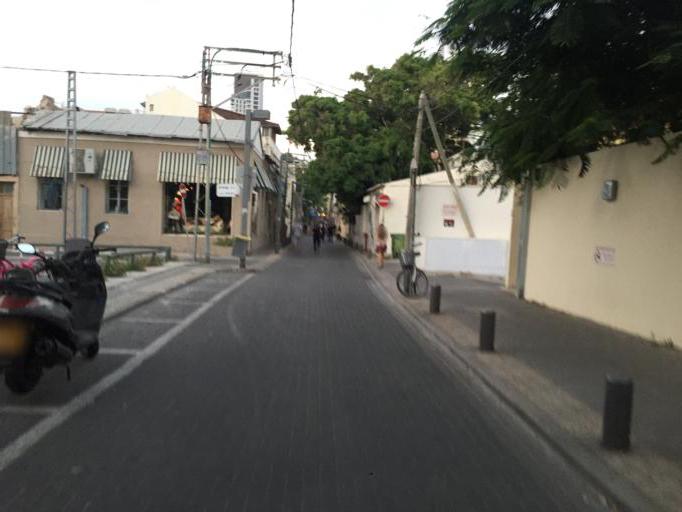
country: IL
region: Tel Aviv
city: Yafo
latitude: 32.0616
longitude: 34.7639
